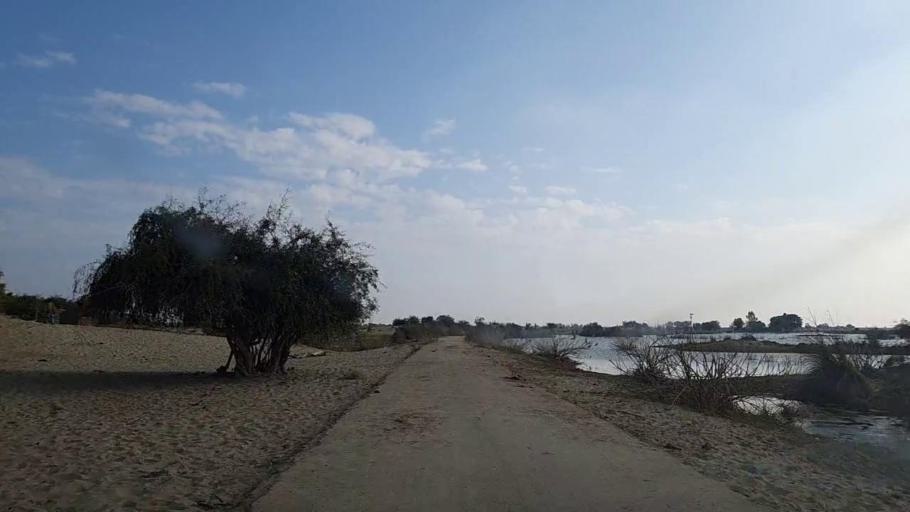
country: PK
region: Sindh
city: Sanghar
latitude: 26.2001
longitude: 69.0297
